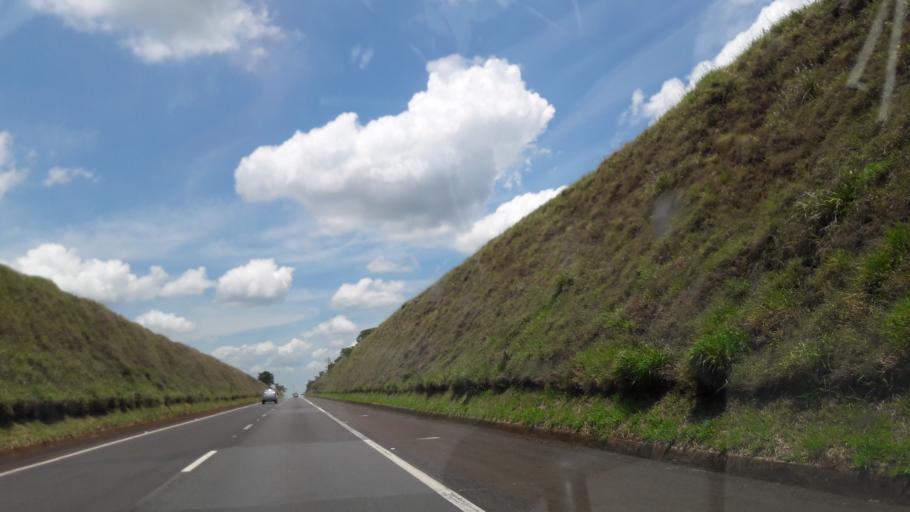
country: BR
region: Sao Paulo
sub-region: Avare
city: Avare
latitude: -22.9552
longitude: -48.8339
